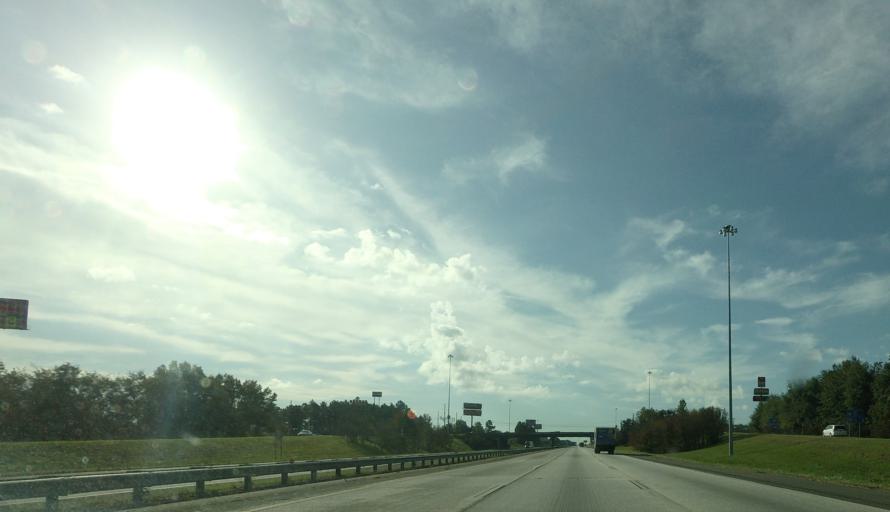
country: US
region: Georgia
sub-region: Peach County
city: Byron
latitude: 32.6146
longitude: -83.7430
